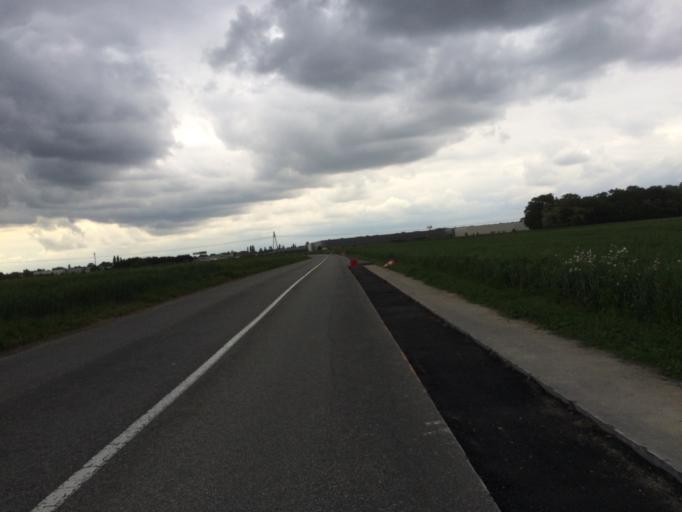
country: FR
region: Ile-de-France
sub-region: Departement de l'Essonne
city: Le Plessis-Pate
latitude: 48.6146
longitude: 2.3437
